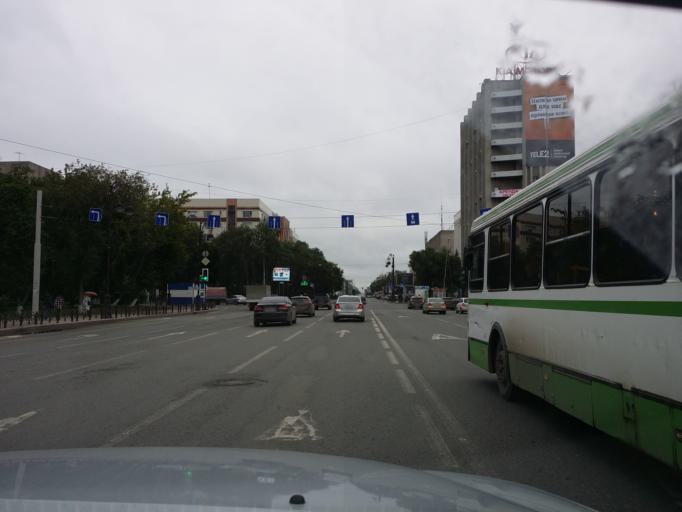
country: RU
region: Tjumen
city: Tyumen
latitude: 57.1478
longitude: 65.5506
